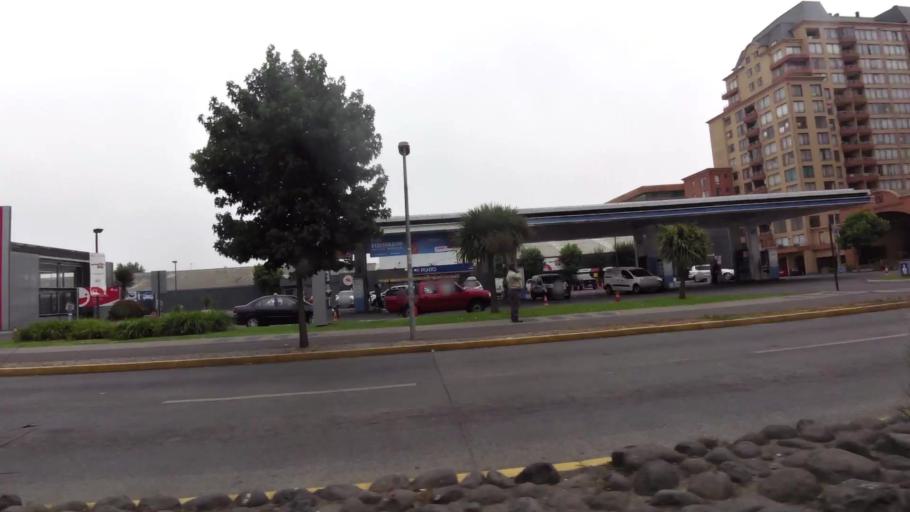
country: CL
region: Biobio
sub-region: Provincia de Concepcion
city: Concepcion
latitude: -36.8324
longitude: -73.0573
